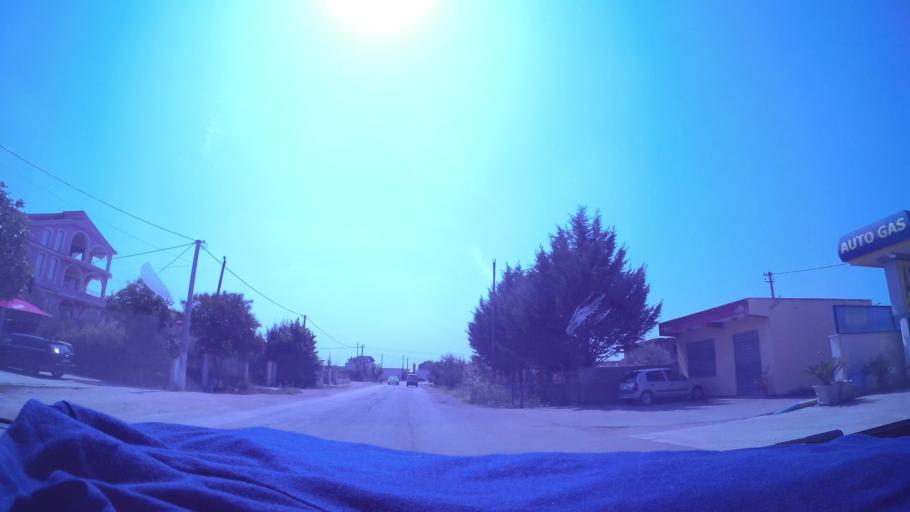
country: AL
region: Durres
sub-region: Rrethi i Durresit
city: Xhafzotaj
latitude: 41.3525
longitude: 19.5465
